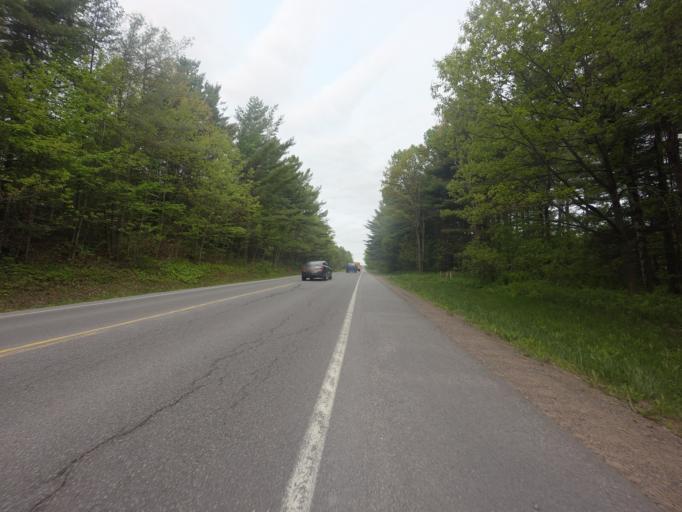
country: US
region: New York
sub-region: Jefferson County
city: Carthage
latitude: 44.0335
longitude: -75.6254
